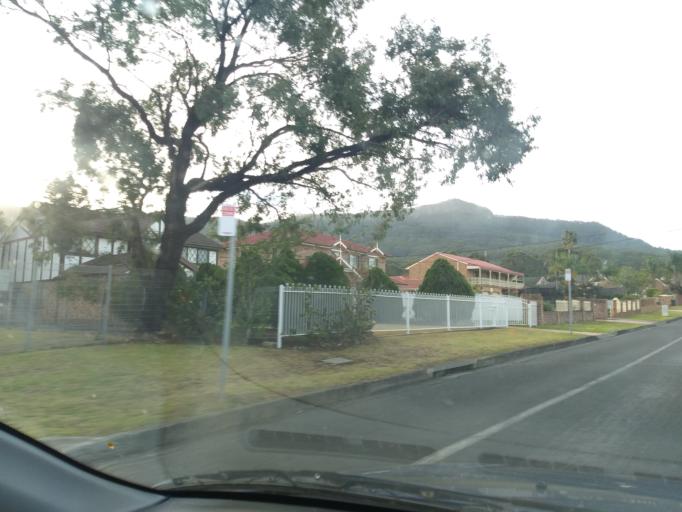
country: AU
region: New South Wales
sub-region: Wollongong
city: Mount Ousley
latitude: -34.3837
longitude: 150.8817
